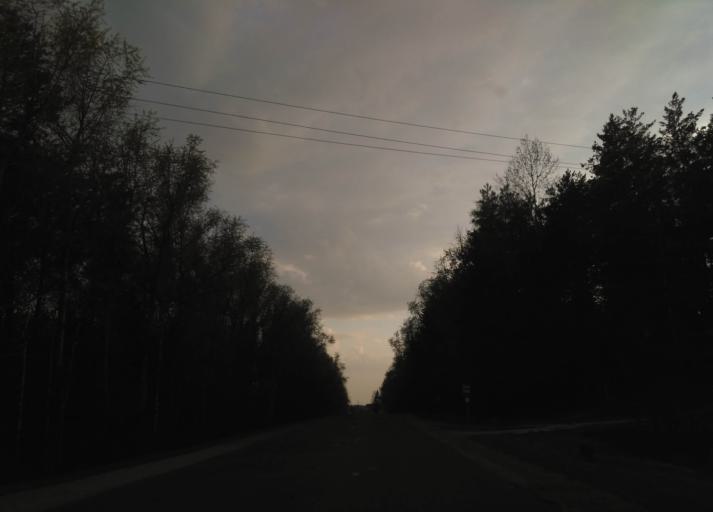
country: BY
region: Minsk
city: Loshnitsa
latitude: 54.4165
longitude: 28.6359
